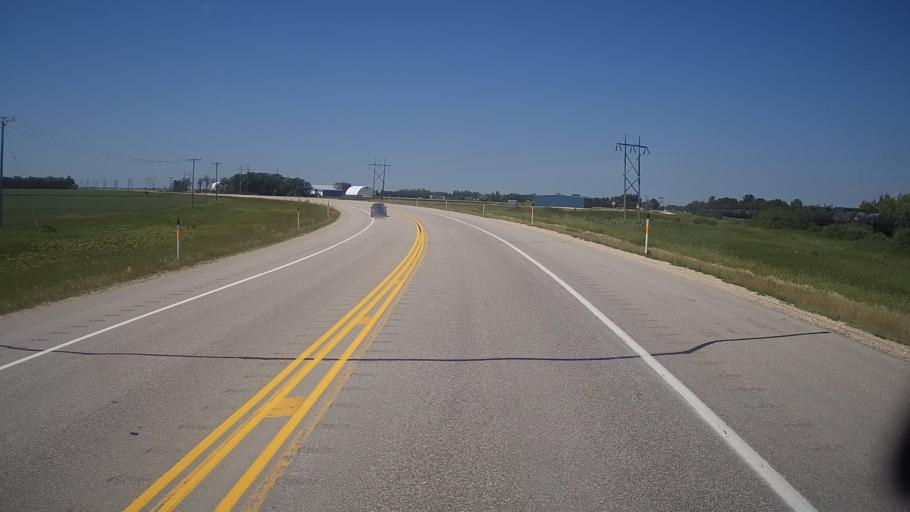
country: CA
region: Manitoba
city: Stonewall
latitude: 50.1220
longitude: -97.5315
